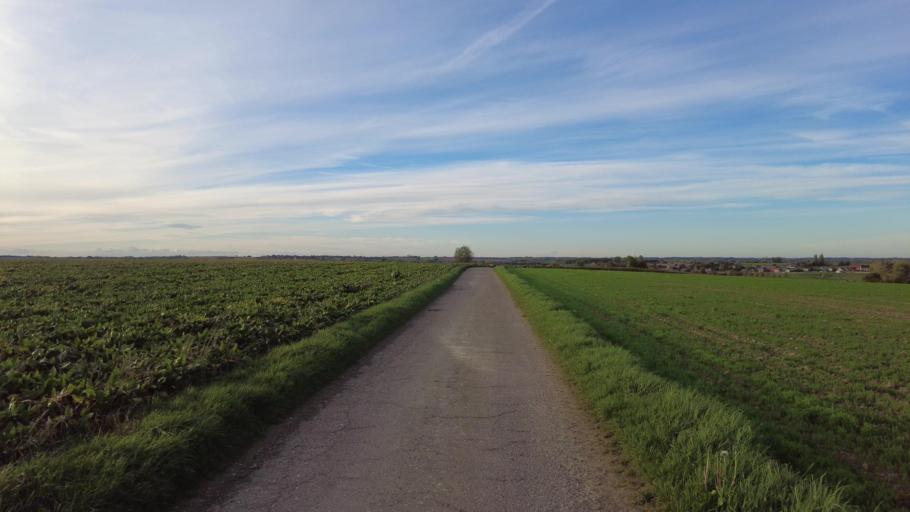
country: BE
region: Flanders
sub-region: Provincie Vlaams-Brabant
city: Hoegaarden
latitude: 50.7568
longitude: 4.9299
